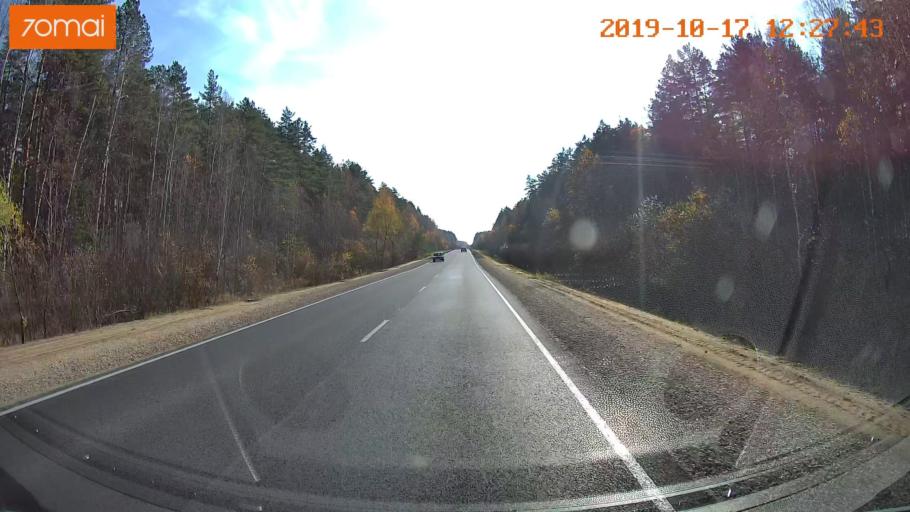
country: RU
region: Rjazan
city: Syntul
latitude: 54.9995
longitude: 41.2647
